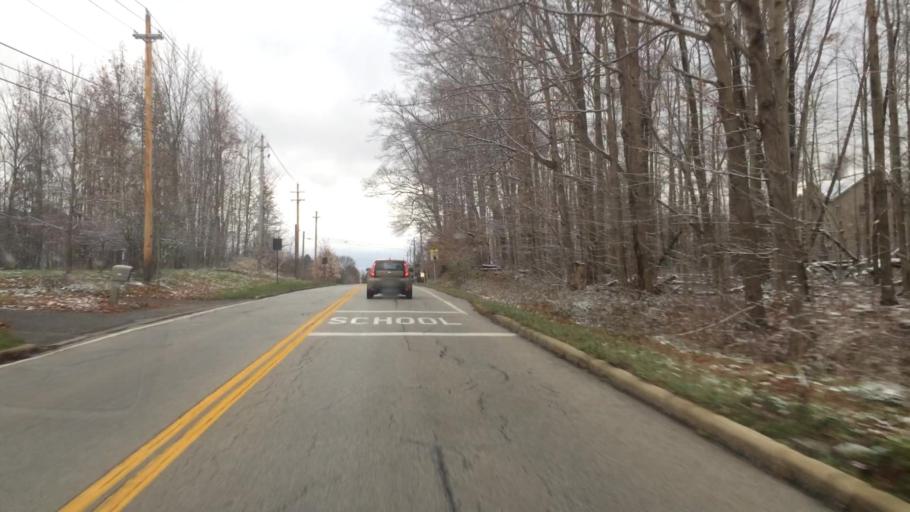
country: US
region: Ohio
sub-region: Summit County
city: Hudson
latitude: 41.2480
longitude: -81.4111
